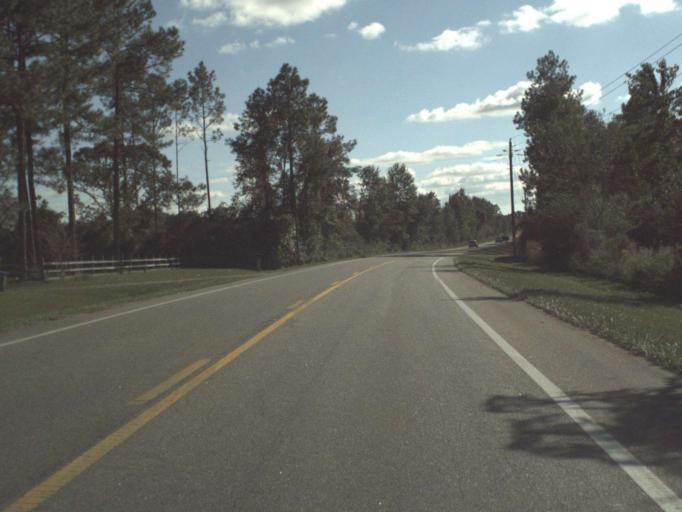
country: US
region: Florida
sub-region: Gulf County
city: Wewahitchka
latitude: 30.1724
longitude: -85.2057
